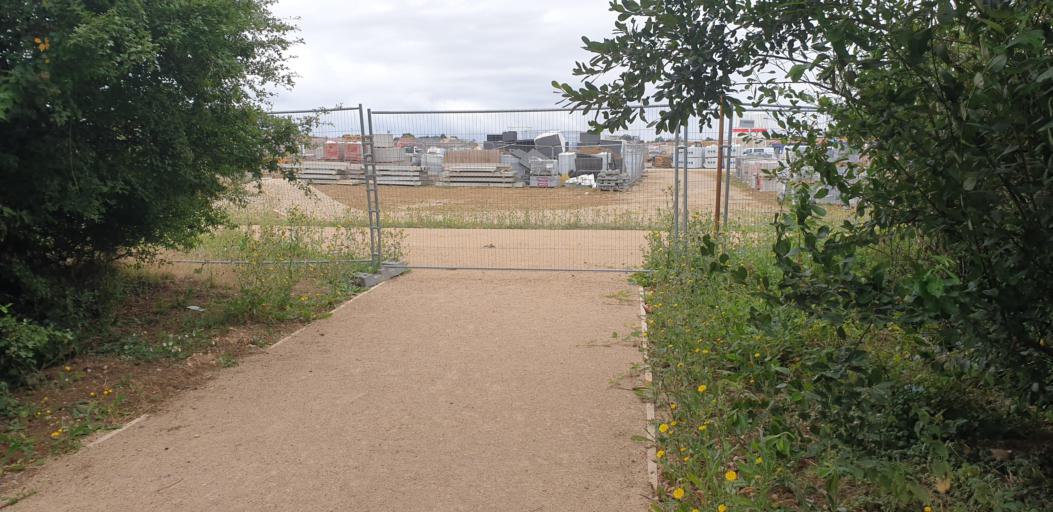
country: GB
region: England
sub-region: Oxfordshire
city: Abingdon
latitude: 51.6941
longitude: -1.2788
